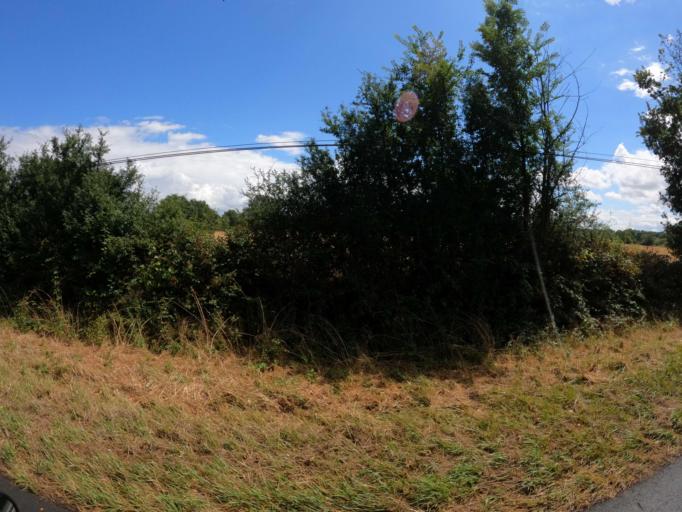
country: FR
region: Pays de la Loire
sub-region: Departement de Maine-et-Loire
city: Feneu
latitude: 47.5907
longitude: -0.5897
